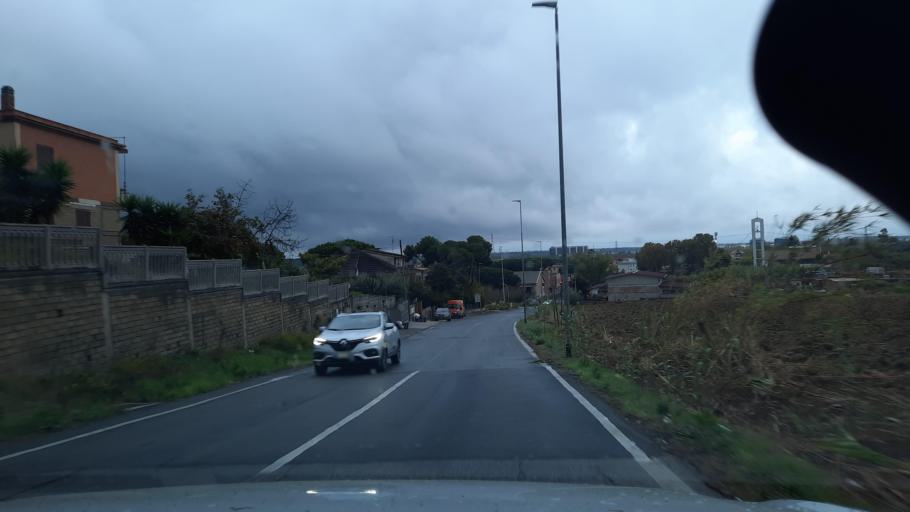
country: IT
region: Latium
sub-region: Citta metropolitana di Roma Capitale
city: Ponte Galeria-La Pisana
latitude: 41.8214
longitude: 12.3508
